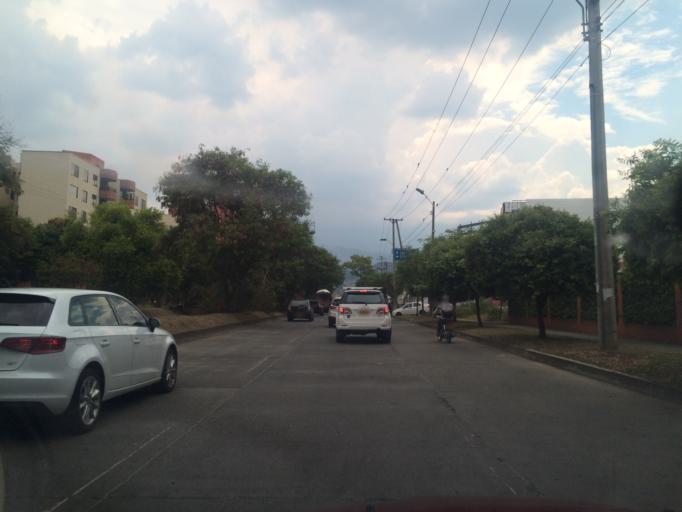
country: CO
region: Valle del Cauca
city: Cali
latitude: 3.3875
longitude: -76.5350
